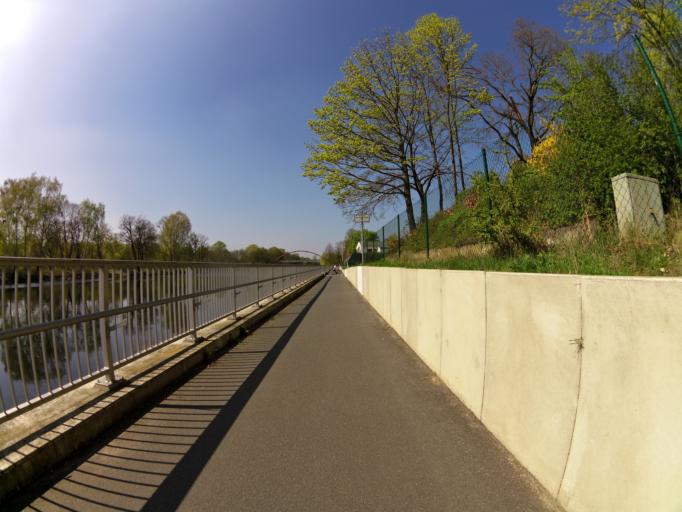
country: DE
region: Berlin
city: Haselhorst
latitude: 52.5563
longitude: 13.2406
